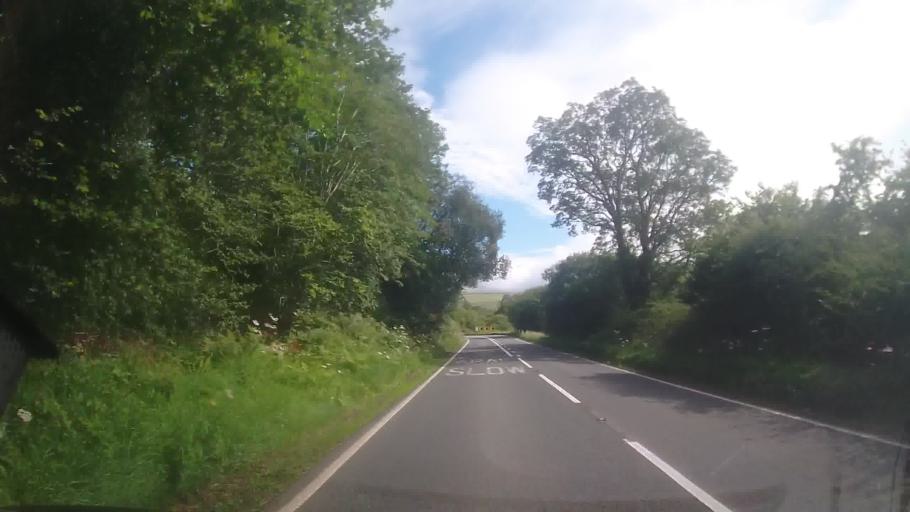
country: GB
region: Wales
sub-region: Conwy
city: Llangwm
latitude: 53.0085
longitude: -3.5519
